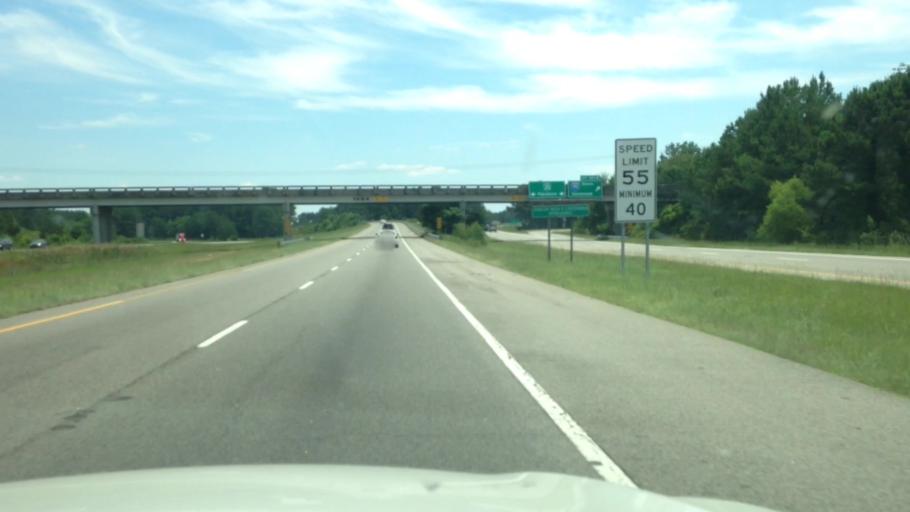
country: US
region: South Carolina
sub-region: Florence County
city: Florence
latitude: 34.1968
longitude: -79.8510
